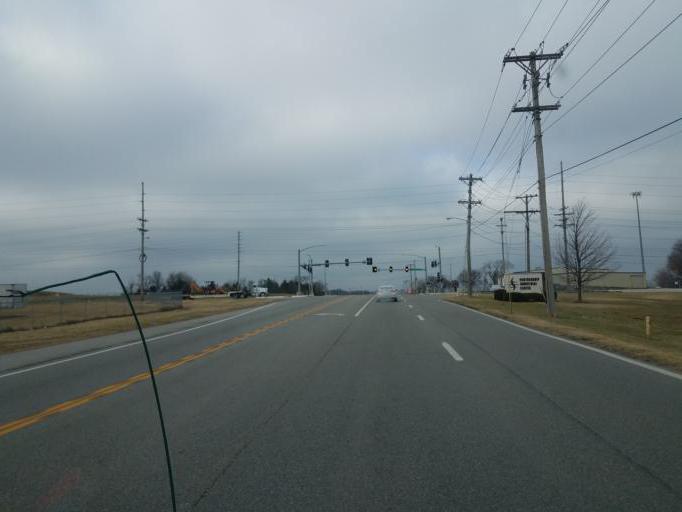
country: US
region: Missouri
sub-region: Greene County
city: Springfield
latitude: 37.2386
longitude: -93.2144
